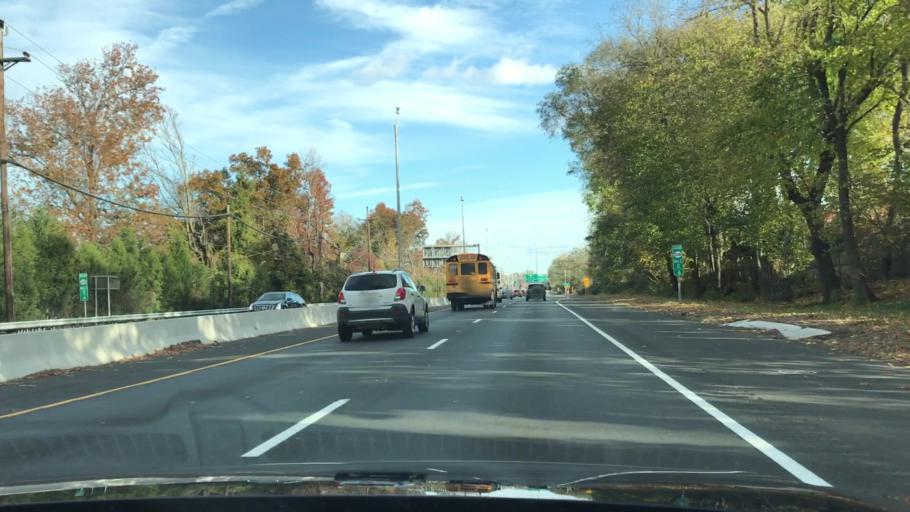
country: US
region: New Jersey
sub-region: Bergen County
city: Elmwood Park
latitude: 40.9291
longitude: -74.1025
